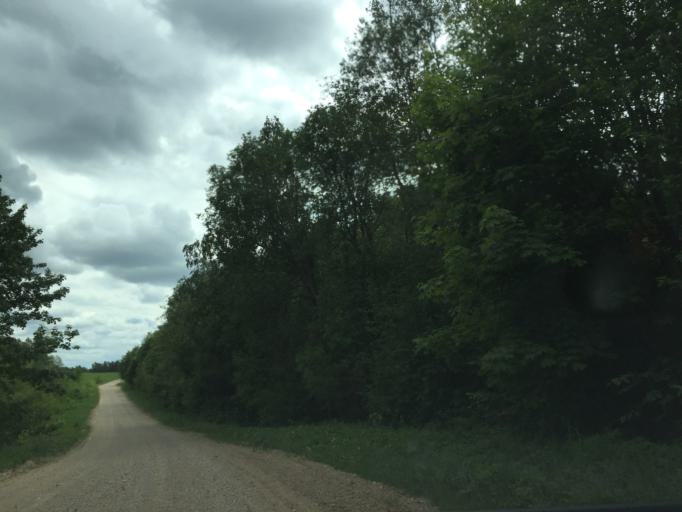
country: LV
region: Dagda
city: Dagda
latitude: 56.0467
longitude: 27.6415
